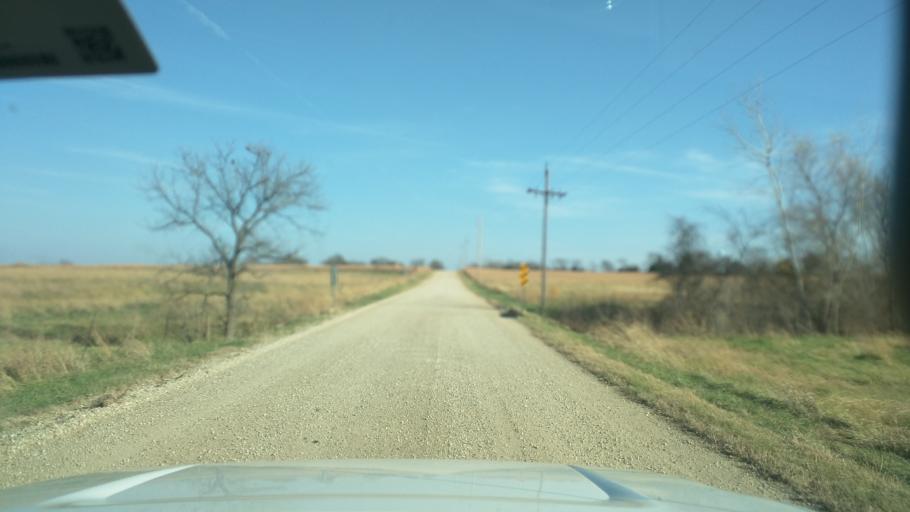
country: US
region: Kansas
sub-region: Lyon County
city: Emporia
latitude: 38.2890
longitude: -96.1800
